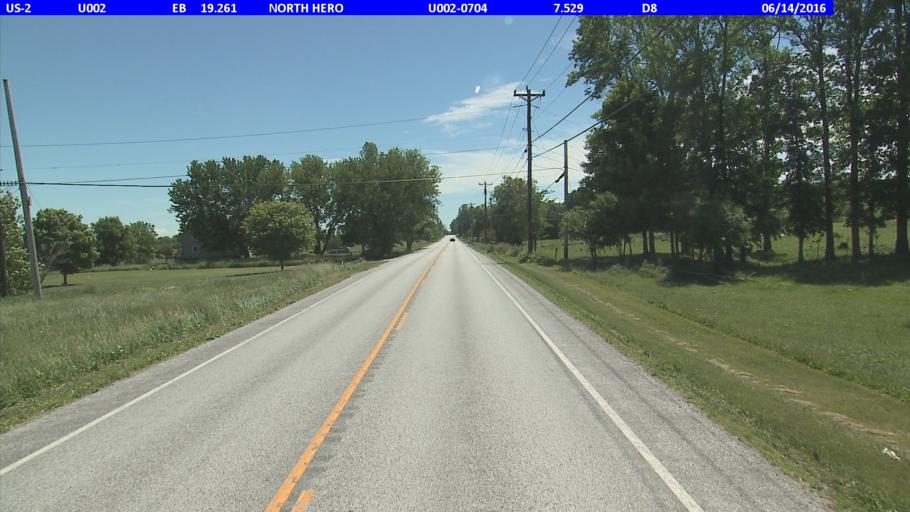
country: US
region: Vermont
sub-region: Grand Isle County
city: North Hero
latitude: 44.7912
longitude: -73.2927
